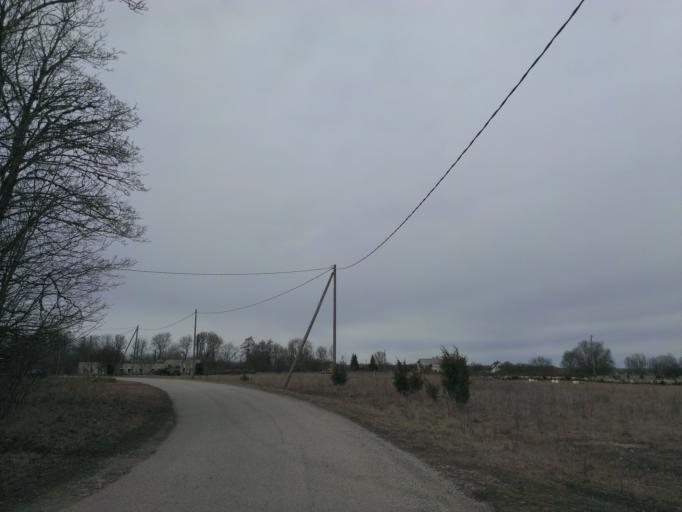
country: EE
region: Laeaene
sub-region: Lihula vald
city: Lihula
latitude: 58.5792
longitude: 23.5406
